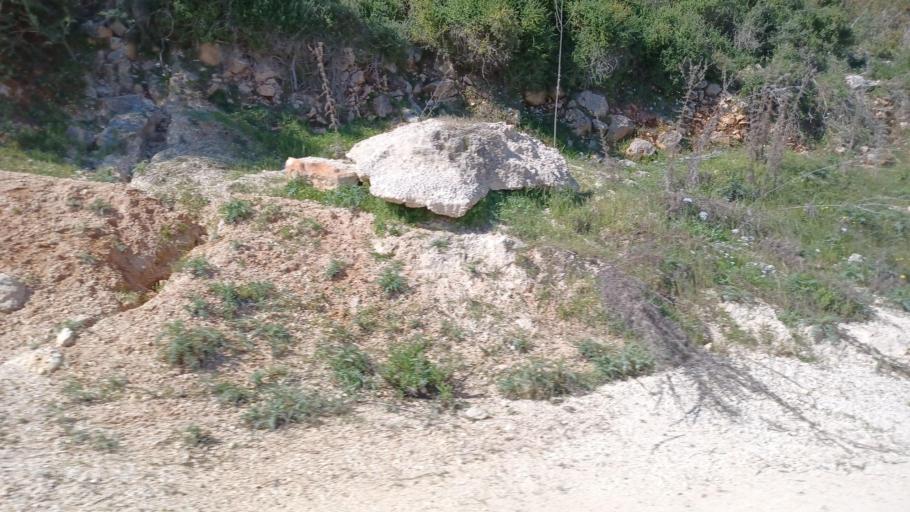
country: CY
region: Pafos
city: Polis
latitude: 35.0019
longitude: 32.3932
